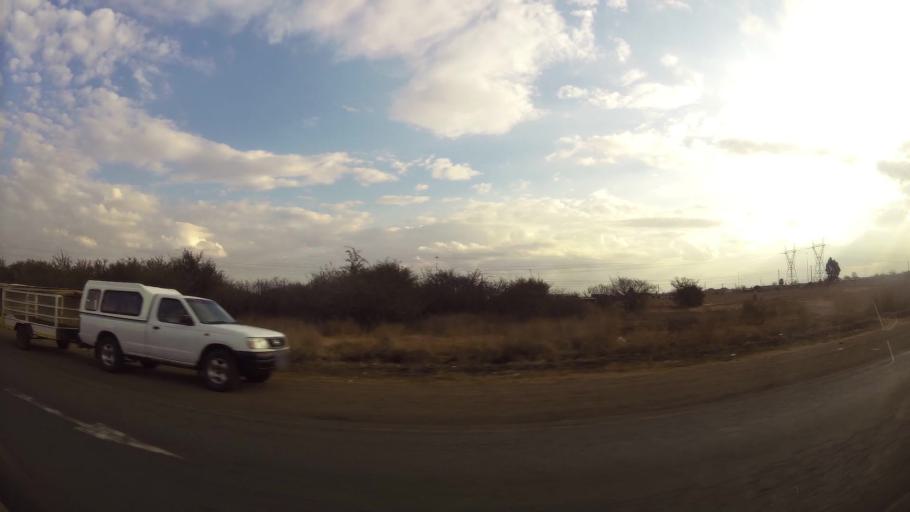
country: ZA
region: Gauteng
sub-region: Sedibeng District Municipality
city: Vanderbijlpark
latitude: -26.6876
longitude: 27.8010
